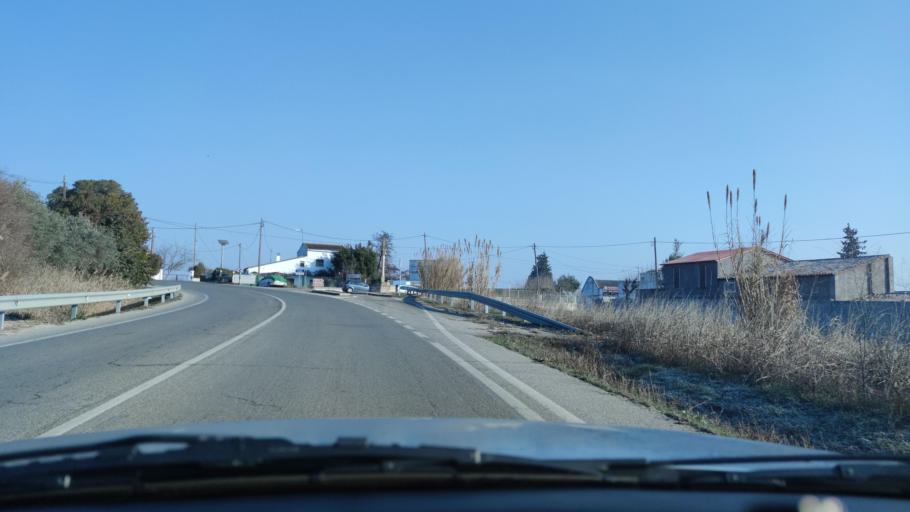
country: ES
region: Catalonia
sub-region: Provincia de Lleida
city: Lleida
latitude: 41.6387
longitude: 0.6372
